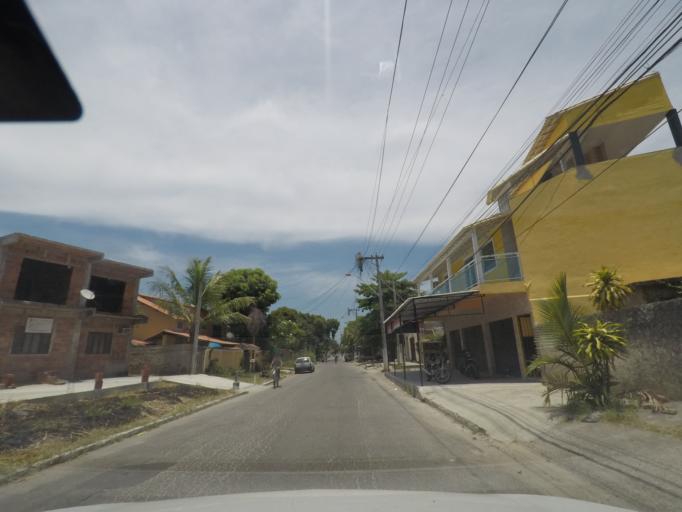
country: BR
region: Rio de Janeiro
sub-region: Marica
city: Marica
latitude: -22.9093
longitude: -42.8366
